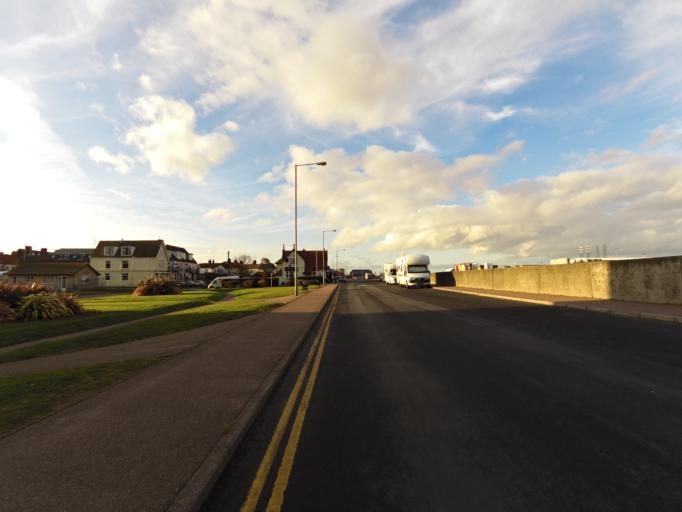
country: GB
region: England
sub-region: Norfolk
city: Gorleston-on-Sea
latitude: 52.5726
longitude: 1.7322
